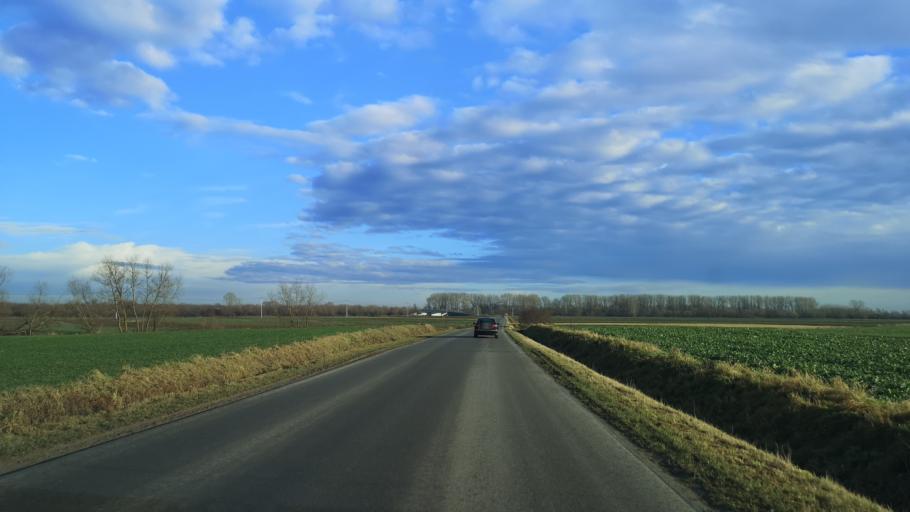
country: PL
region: Subcarpathian Voivodeship
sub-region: Powiat lezajski
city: Wierzawice
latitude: 50.2468
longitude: 22.4880
